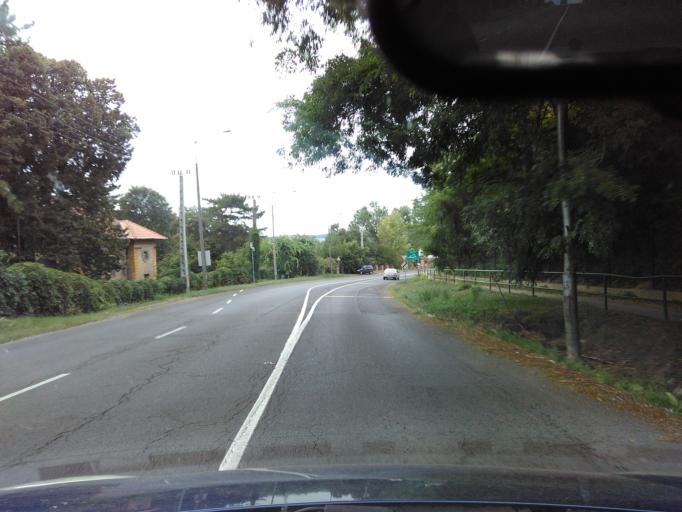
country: HU
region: Pest
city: Aszod
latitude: 47.6509
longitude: 19.4921
